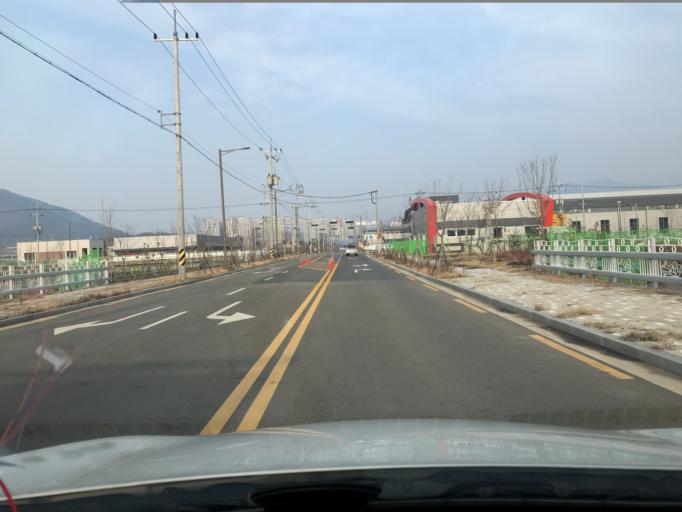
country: KR
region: Gyeongsangnam-do
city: Changnyeong
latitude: 35.6460
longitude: 128.4063
